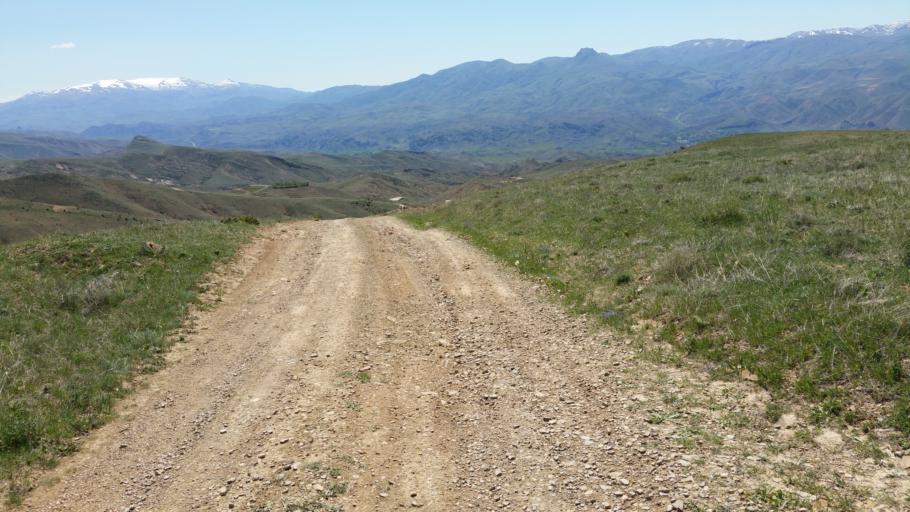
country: AM
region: Vayots' Dzori Marz
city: Vernashen
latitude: 39.8013
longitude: 45.3606
